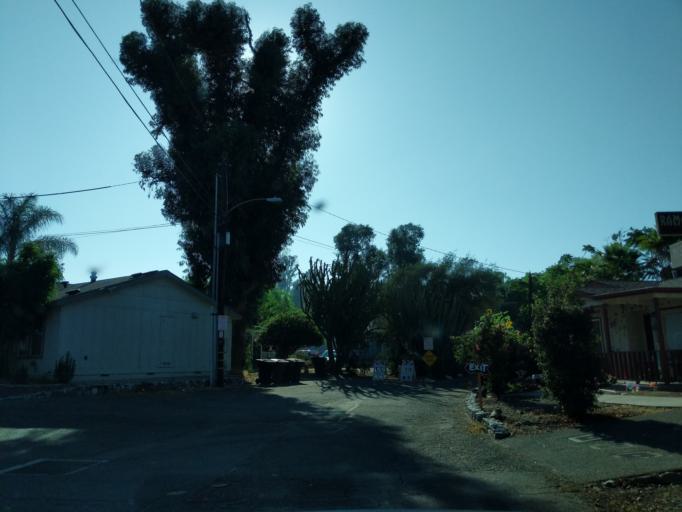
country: US
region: California
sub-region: Orange County
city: San Juan Capistrano
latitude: 33.5034
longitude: -117.6665
